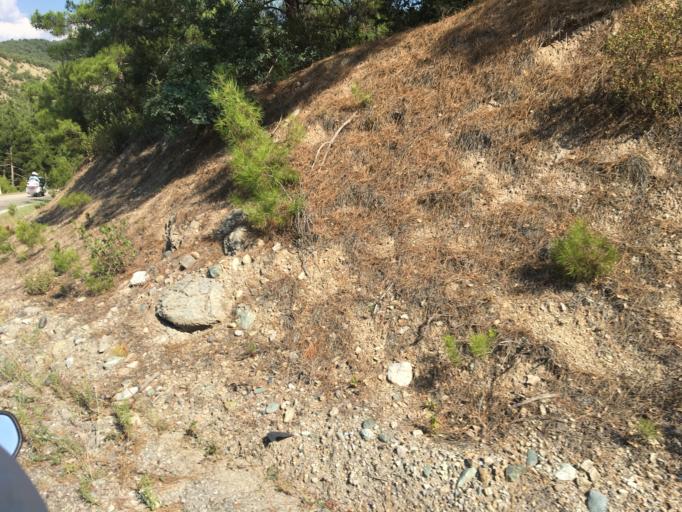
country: TR
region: Ankara
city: Beydili
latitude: 40.0676
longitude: 30.9117
